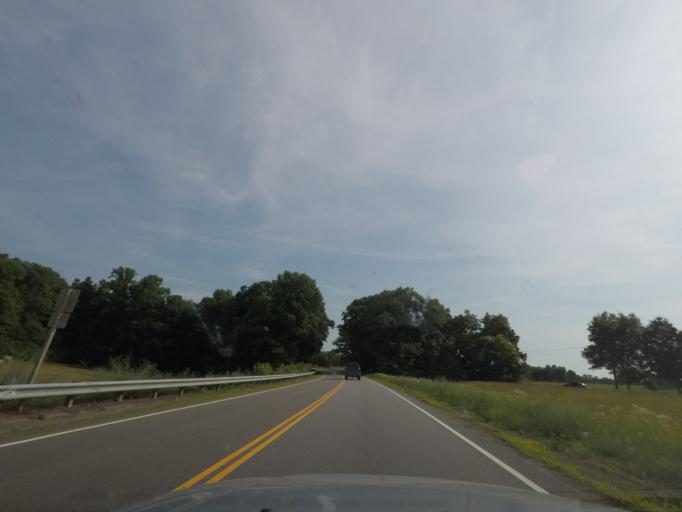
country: US
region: Virginia
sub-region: Mecklenburg County
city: Chase City
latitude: 36.8032
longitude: -78.6039
